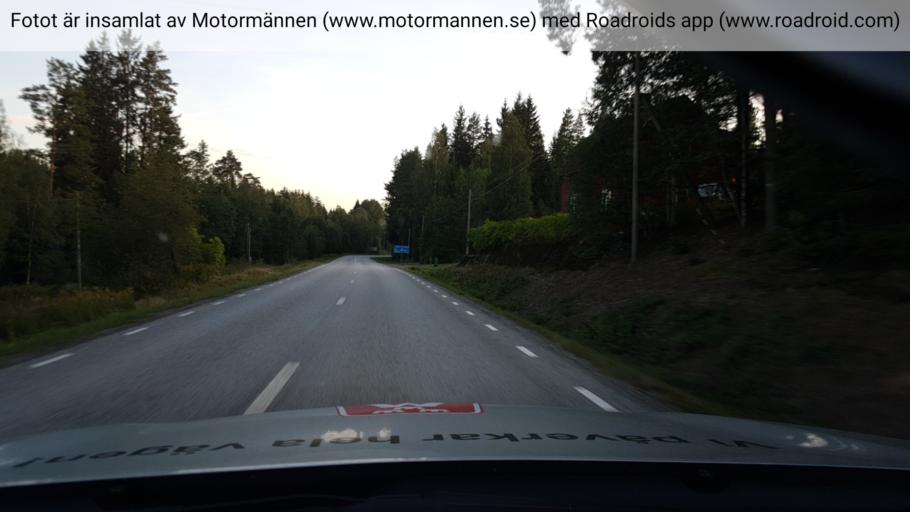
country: SE
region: OErebro
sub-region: Ljusnarsbergs Kommun
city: Kopparberg
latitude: 59.8743
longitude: 15.0521
